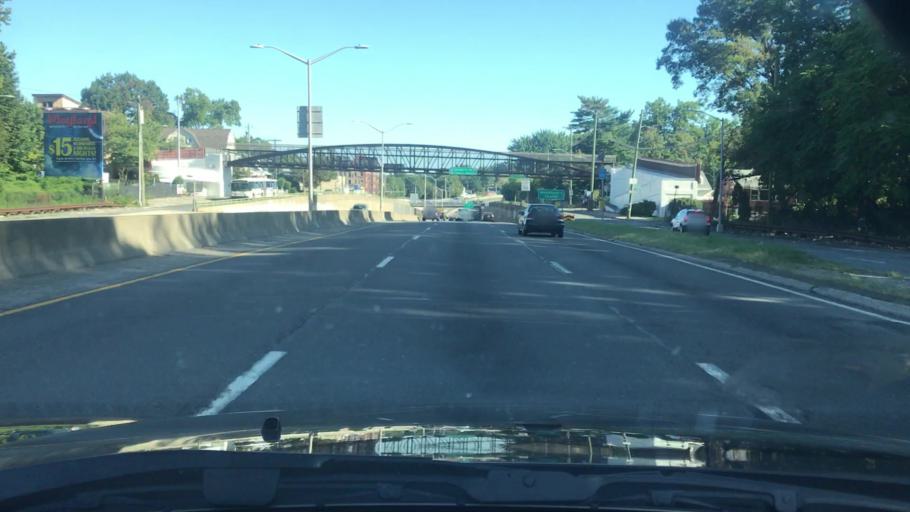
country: US
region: New York
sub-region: Westchester County
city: Yonkers
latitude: 40.9052
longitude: -73.8781
